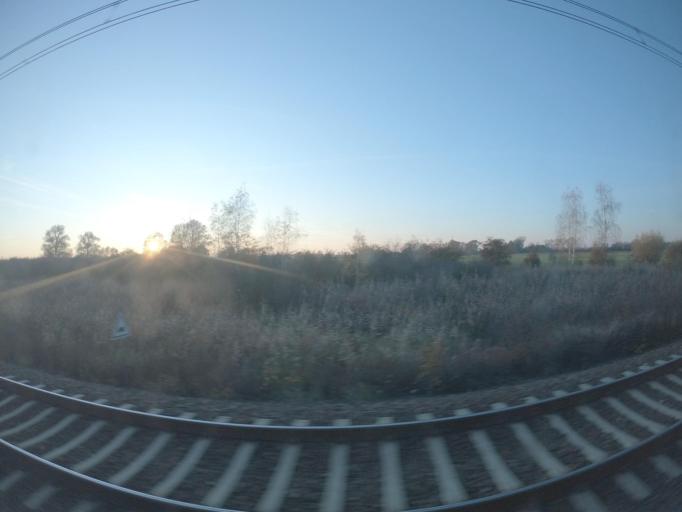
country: PL
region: Lubusz
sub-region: Powiat slubicki
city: Gorzyca
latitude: 52.5388
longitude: 14.6508
